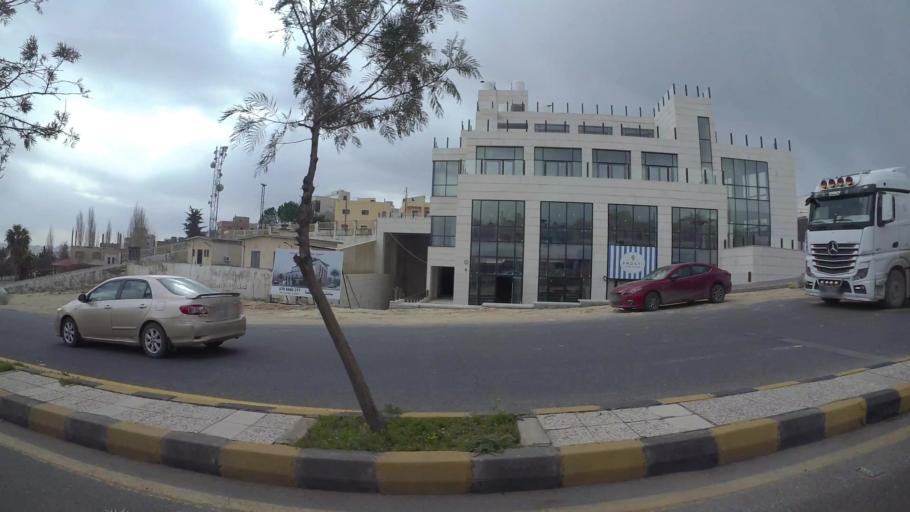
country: JO
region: Amman
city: Wadi as Sir
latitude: 31.9924
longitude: 35.8142
